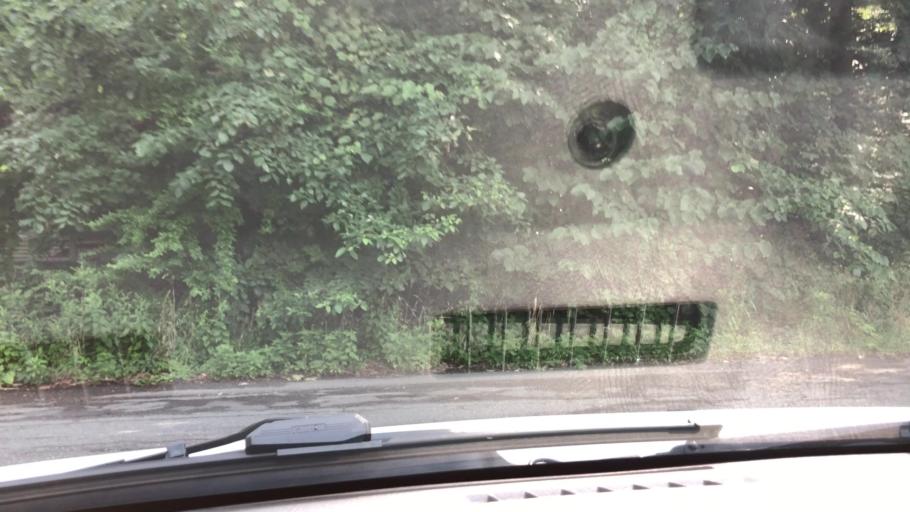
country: US
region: Massachusetts
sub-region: Franklin County
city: Greenfield
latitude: 42.5762
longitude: -72.5945
